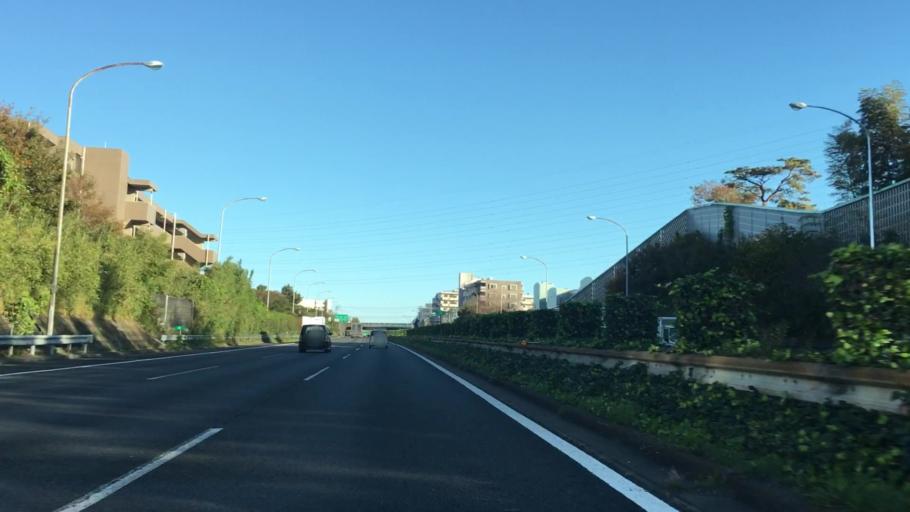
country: JP
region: Tokyo
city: Chofugaoka
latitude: 35.5743
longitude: 139.5641
